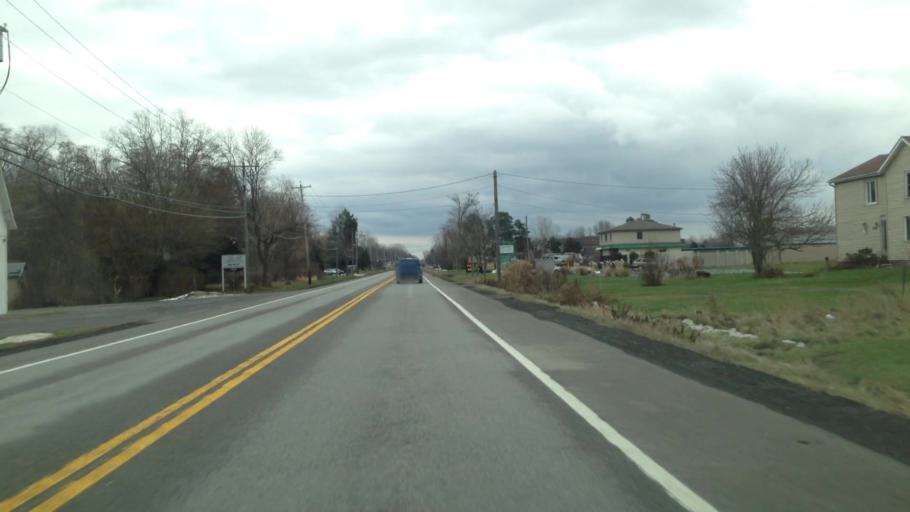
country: US
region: New York
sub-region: Erie County
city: Akron
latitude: 42.9984
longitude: -78.4896
